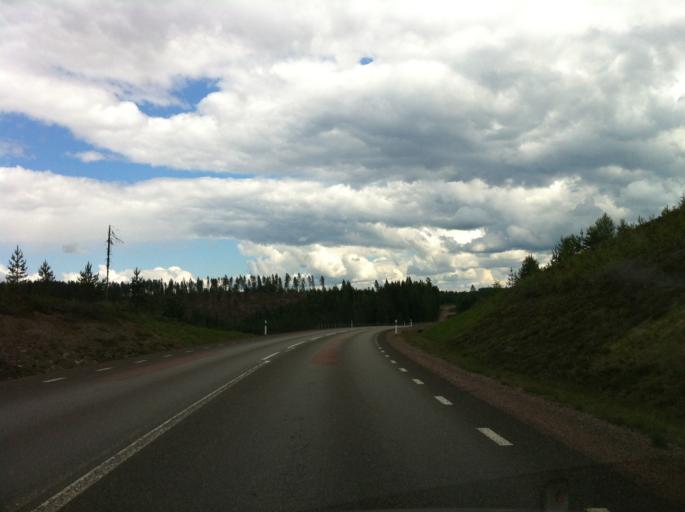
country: SE
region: Dalarna
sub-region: Malung-Saelens kommun
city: Malung
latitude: 60.6109
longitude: 13.5927
